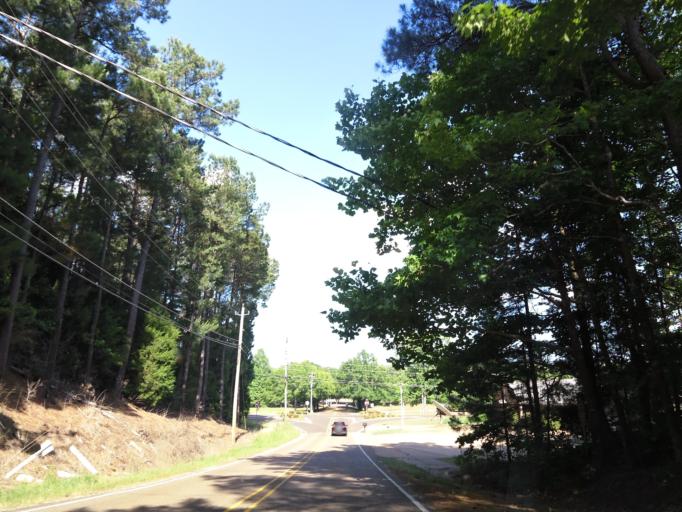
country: US
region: Mississippi
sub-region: Lafayette County
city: Oxford
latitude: 34.3294
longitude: -89.5179
